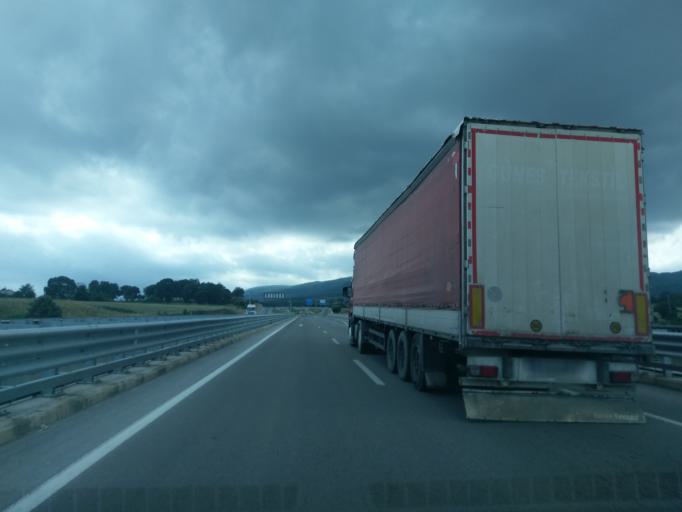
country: TR
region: Sinop
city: Gerze
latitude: 41.8177
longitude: 35.1678
